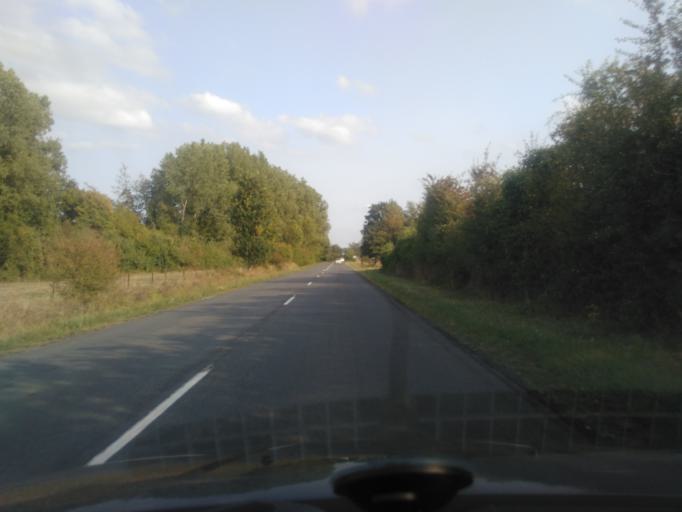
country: FR
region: Picardie
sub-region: Departement de l'Aisne
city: Bruyeres-et-Montberault
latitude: 49.5358
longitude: 3.6475
